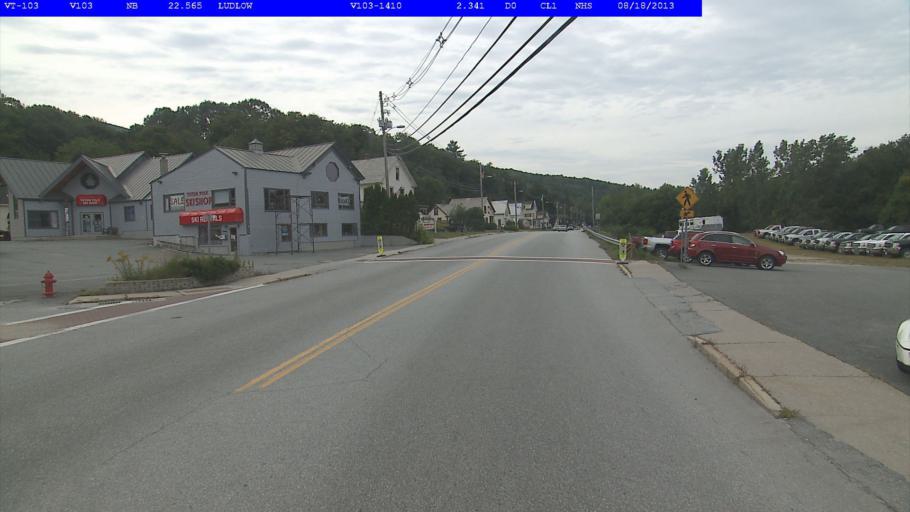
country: US
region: Vermont
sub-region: Windsor County
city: Chester
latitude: 43.3962
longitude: -72.7046
